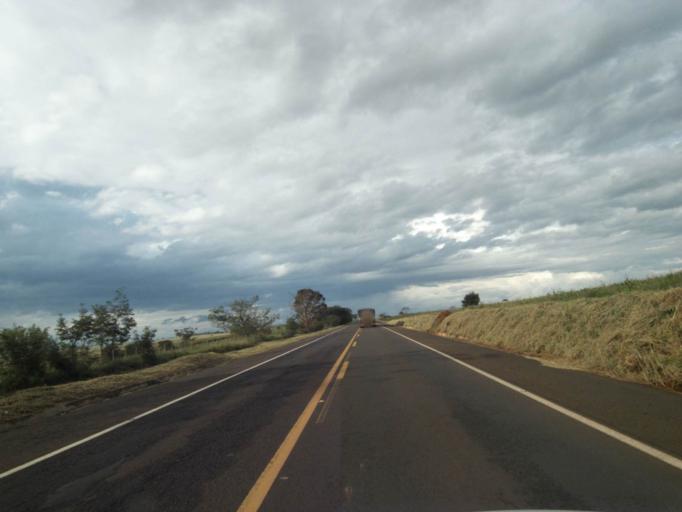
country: PY
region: Canindeyu
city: Salto del Guaira
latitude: -24.0850
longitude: -54.0787
